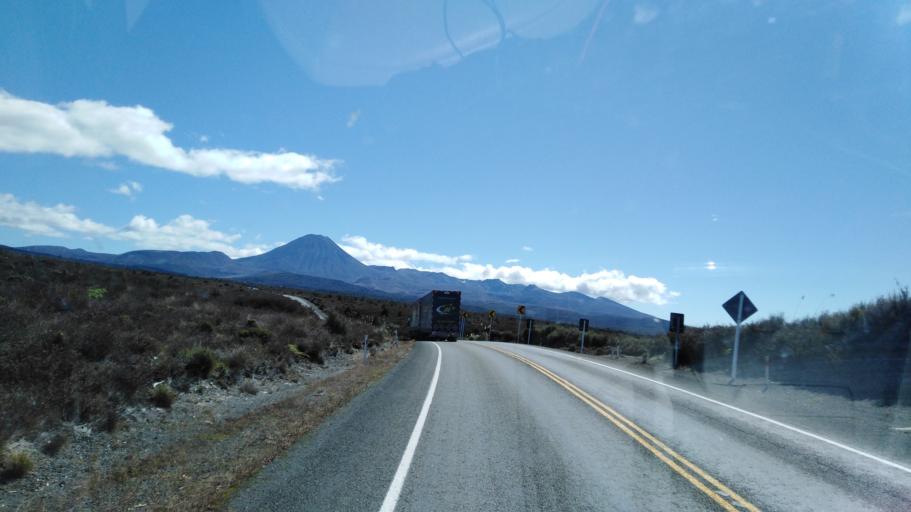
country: NZ
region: Manawatu-Wanganui
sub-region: Ruapehu District
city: Waiouru
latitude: -39.2481
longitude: 175.7351
